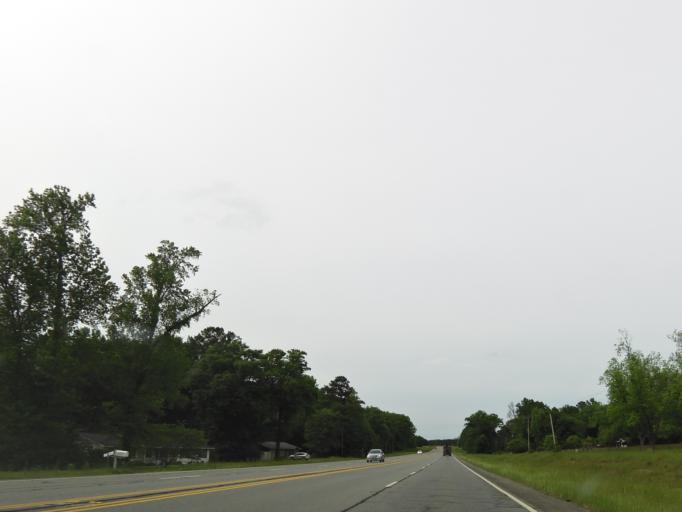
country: US
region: Georgia
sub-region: Bleckley County
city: Cochran
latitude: 32.4486
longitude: -83.3799
